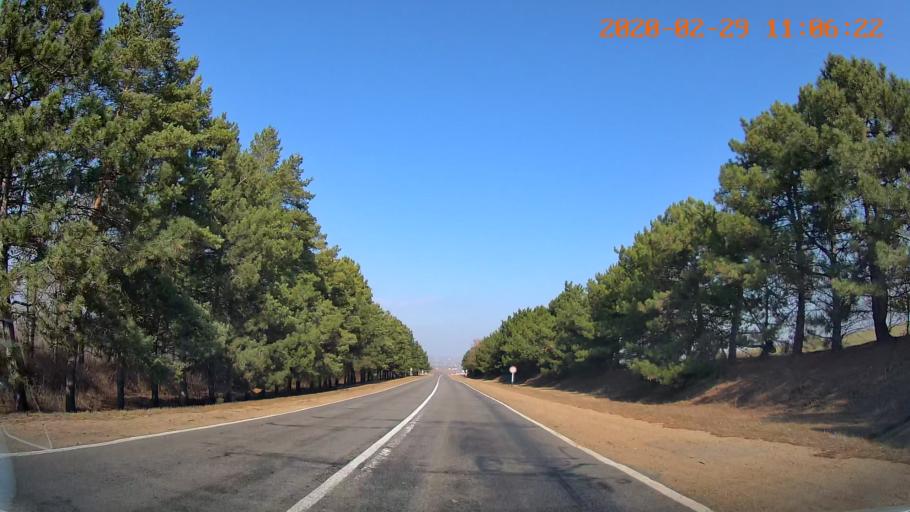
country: MD
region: Criuleni
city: Criuleni
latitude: 47.2137
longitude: 29.1885
